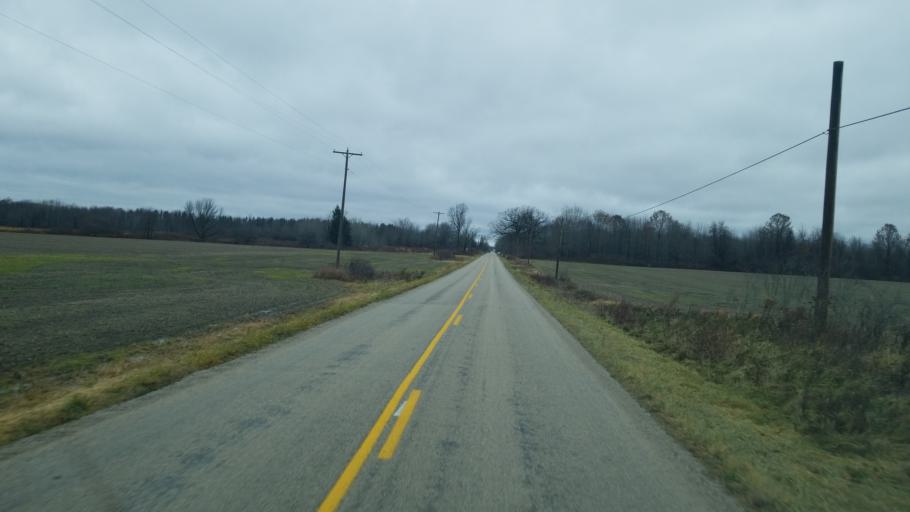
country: US
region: Ohio
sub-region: Ashtabula County
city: Andover
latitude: 41.6605
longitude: -80.6161
